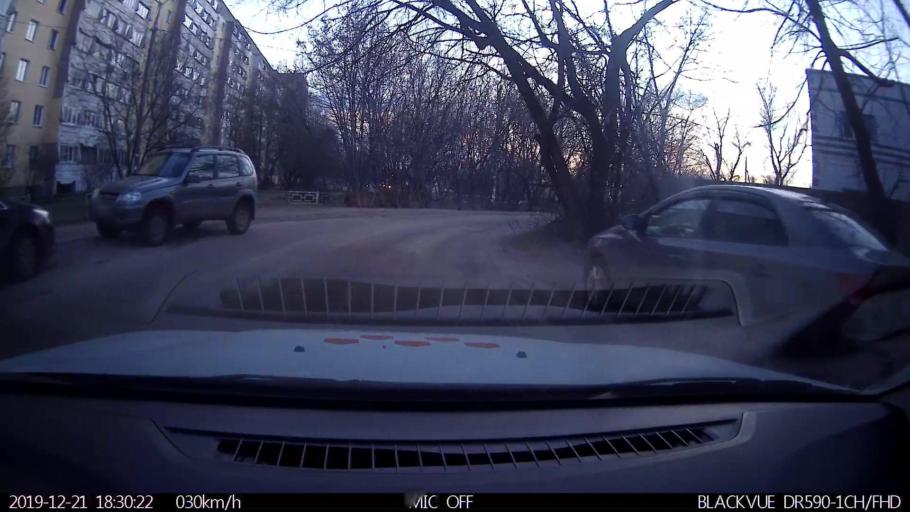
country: RU
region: Nizjnij Novgorod
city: Nizhniy Novgorod
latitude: 56.3355
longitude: 43.9156
